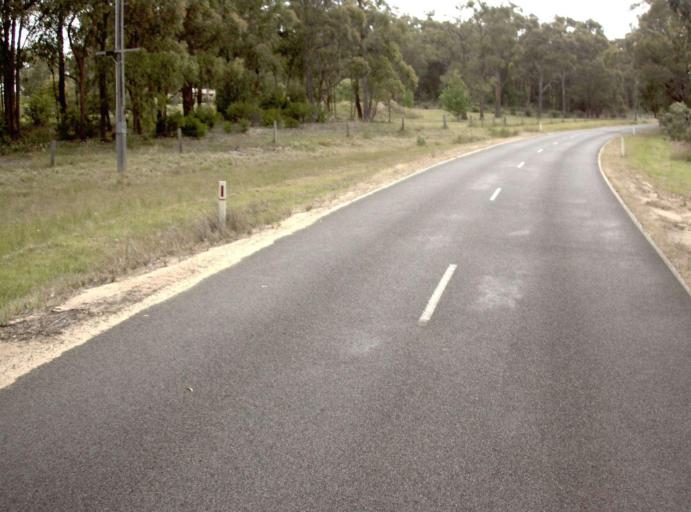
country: AU
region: Victoria
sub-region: Latrobe
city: Traralgon
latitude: -38.3817
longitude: 146.7651
